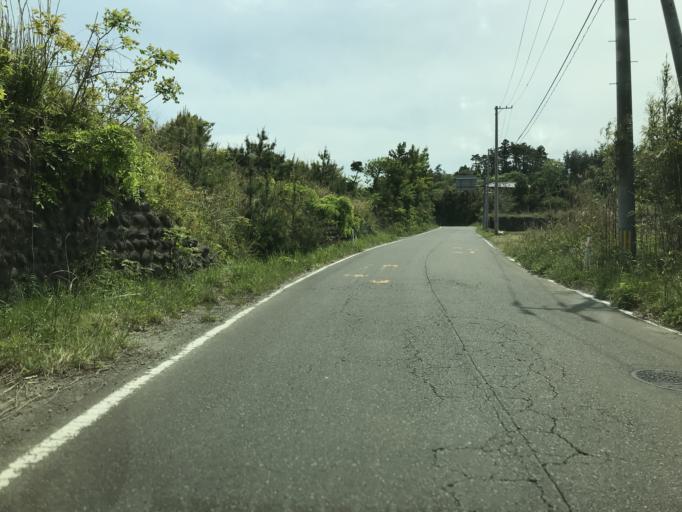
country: JP
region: Miyagi
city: Watari
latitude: 37.8972
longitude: 140.9293
